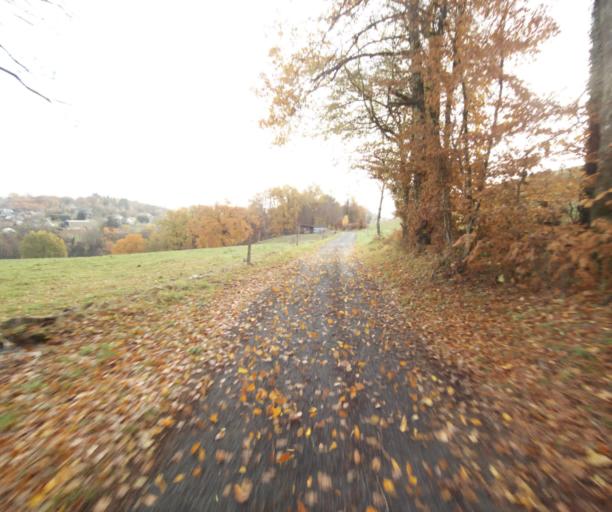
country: FR
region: Limousin
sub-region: Departement de la Correze
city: Cornil
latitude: 45.2215
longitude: 1.6653
